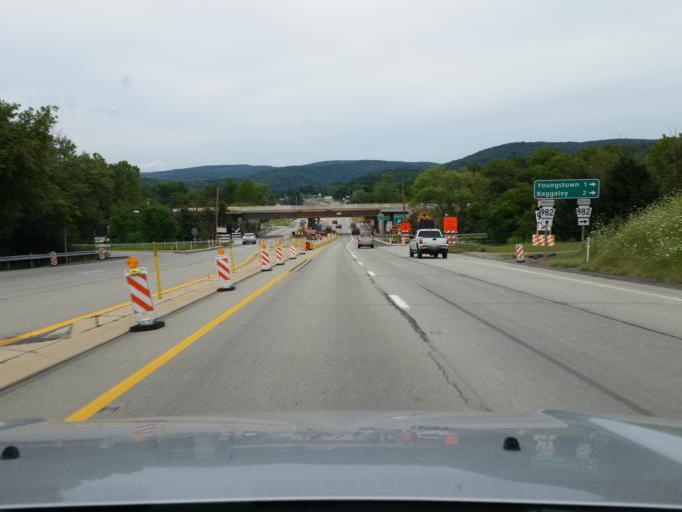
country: US
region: Pennsylvania
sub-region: Westmoreland County
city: Lawson Heights
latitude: 40.2874
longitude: -79.3723
